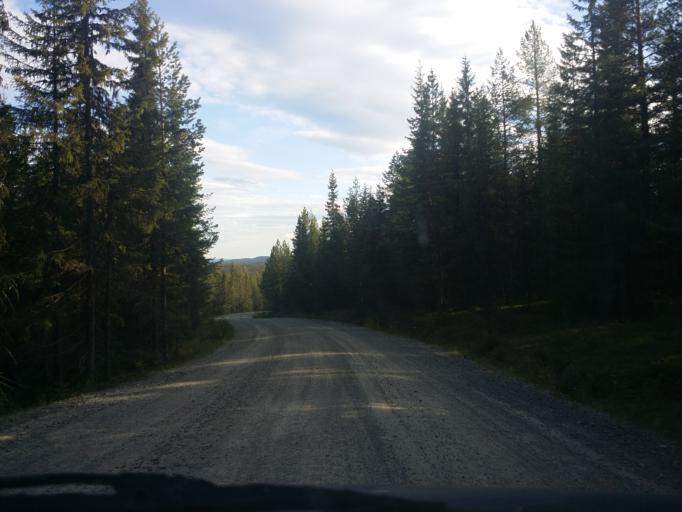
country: NO
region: Hedmark
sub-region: Ringsaker
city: Moelv
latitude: 61.0824
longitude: 10.8421
